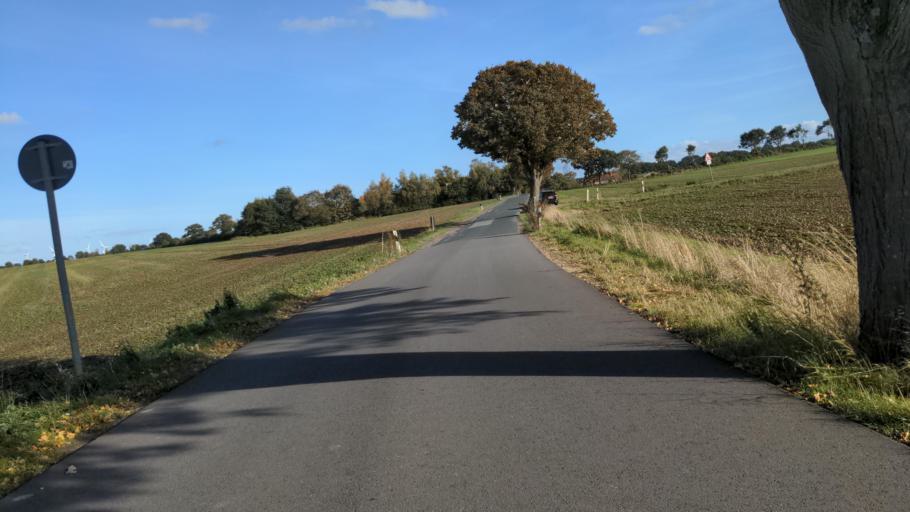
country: DE
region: Schleswig-Holstein
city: Beschendorf
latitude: 54.1995
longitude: 10.8835
